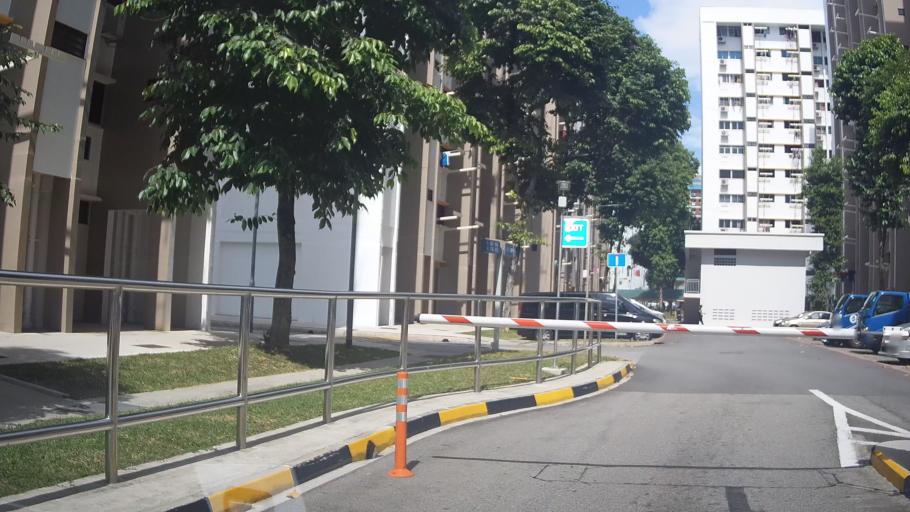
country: SG
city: Singapore
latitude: 1.3458
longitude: 103.9368
